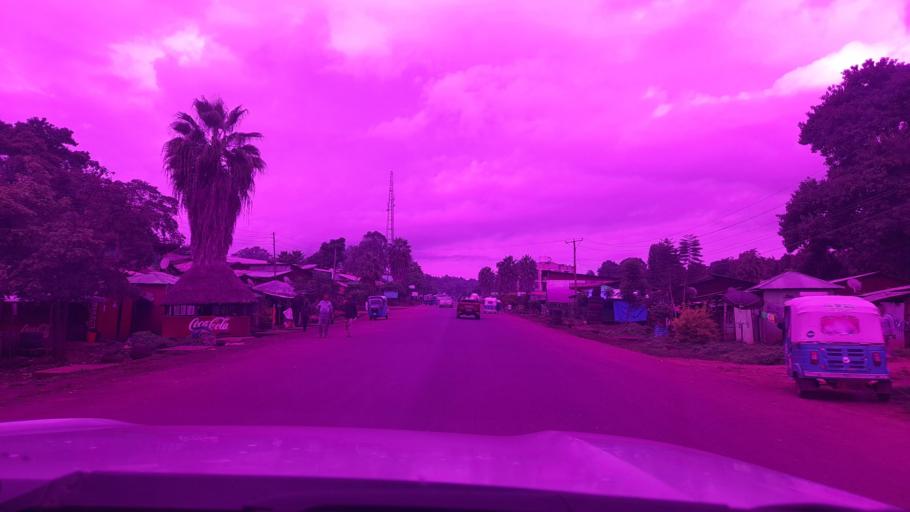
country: ET
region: Oromiya
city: Jima
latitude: 7.9251
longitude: 37.4167
